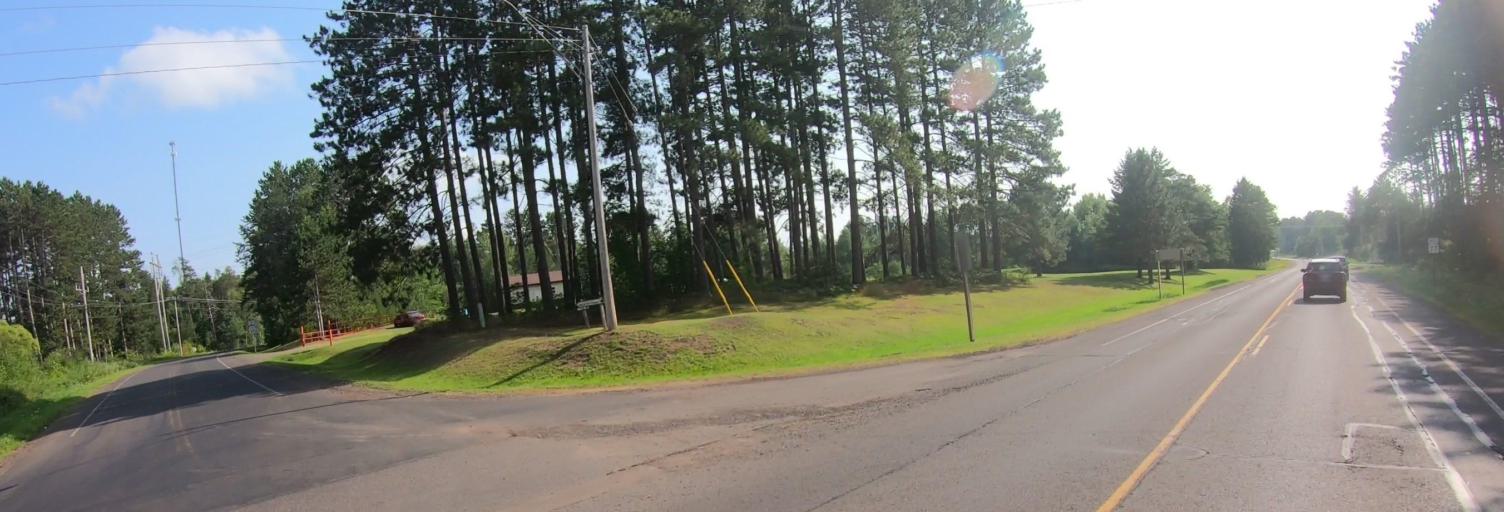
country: US
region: Wisconsin
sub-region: Iron County
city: Hurley
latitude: 46.4465
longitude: -90.1941
